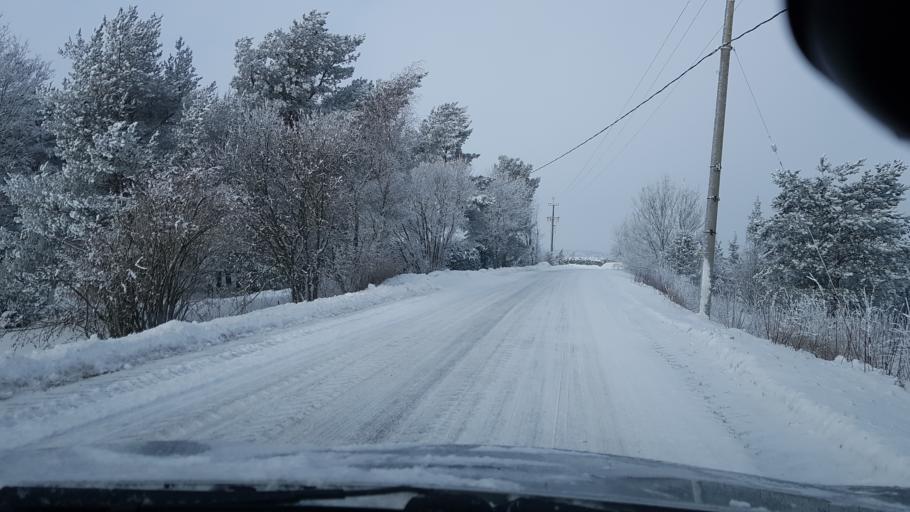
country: EE
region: Harju
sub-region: Keila linn
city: Keila
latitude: 59.3376
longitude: 24.4500
